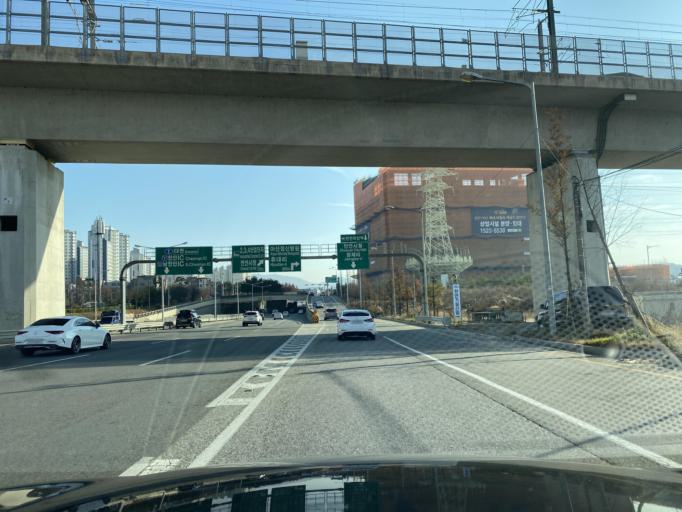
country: KR
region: Chungcheongnam-do
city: Cheonan
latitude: 36.7842
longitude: 127.1066
